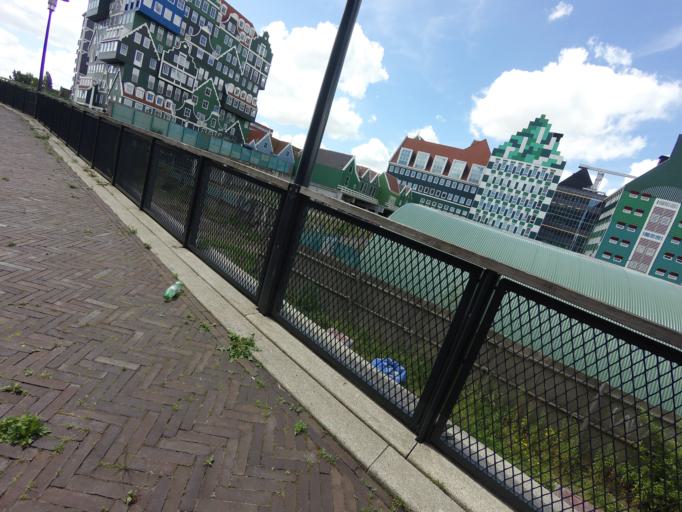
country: NL
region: North Holland
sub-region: Gemeente Zaanstad
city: Zaandam
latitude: 52.4389
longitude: 4.8160
